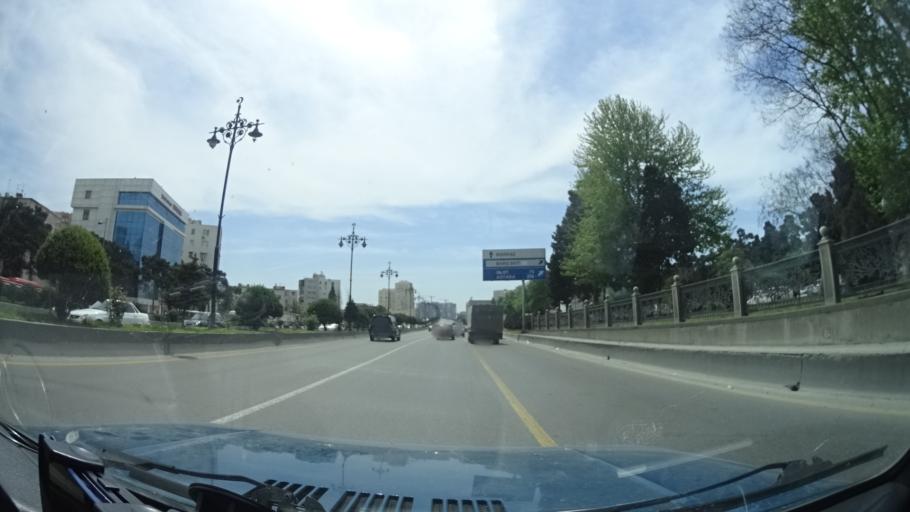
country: AZ
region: Baki
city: Bilajari
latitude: 40.4075
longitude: 49.8056
